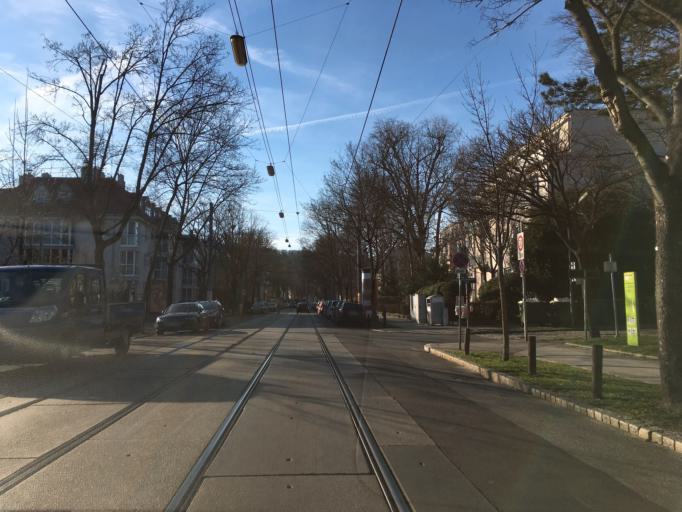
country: AT
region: Vienna
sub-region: Wien Stadt
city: Vienna
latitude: 48.2301
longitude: 16.2988
